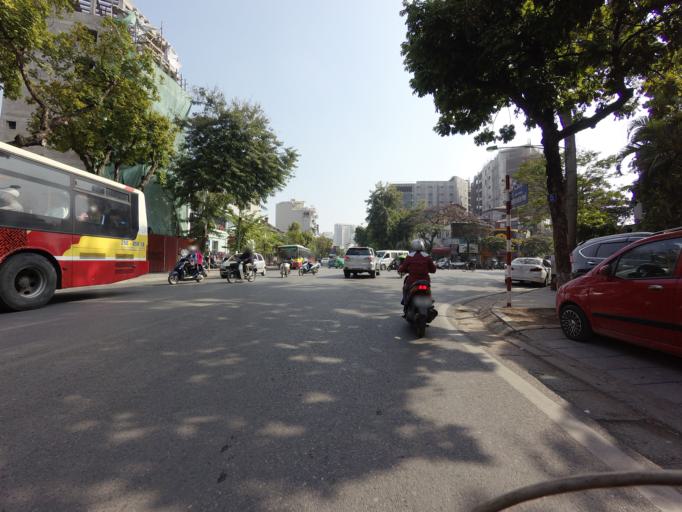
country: VN
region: Ha Noi
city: Hanoi
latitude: 21.0302
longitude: 105.8415
